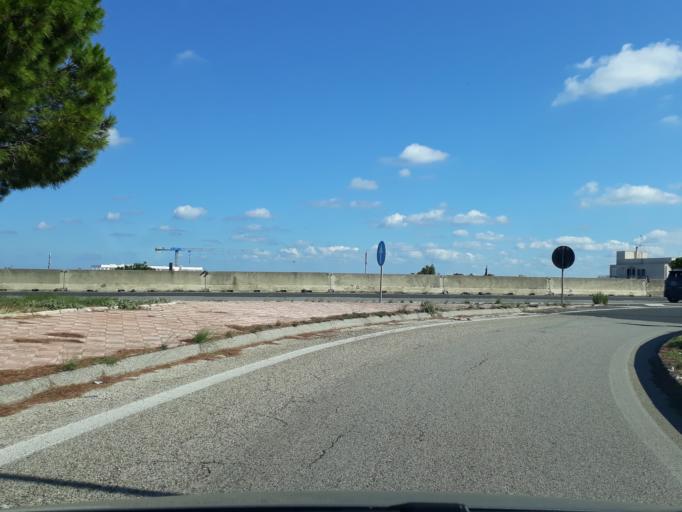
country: IT
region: Apulia
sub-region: Provincia di Bari
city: Mola di Bari
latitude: 41.0512
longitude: 17.0727
